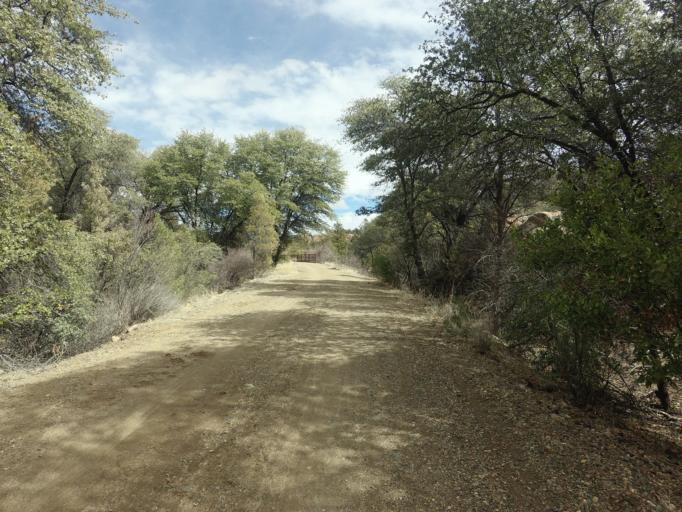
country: US
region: Arizona
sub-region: Yavapai County
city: Prescott Valley
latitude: 34.6042
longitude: -112.3934
